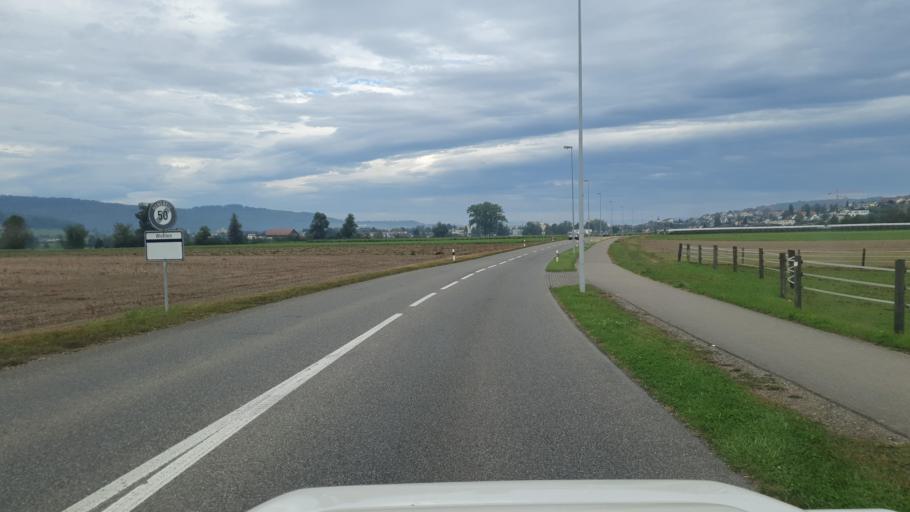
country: CH
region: Aargau
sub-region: Bezirk Muri
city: Waltenschwil
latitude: 47.3382
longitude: 8.2952
